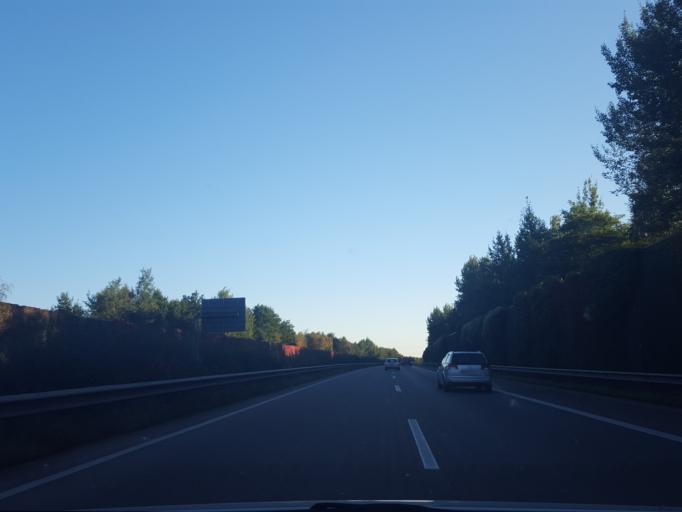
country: DE
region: Lower Saxony
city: Schiffdorf
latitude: 53.5130
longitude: 8.6285
